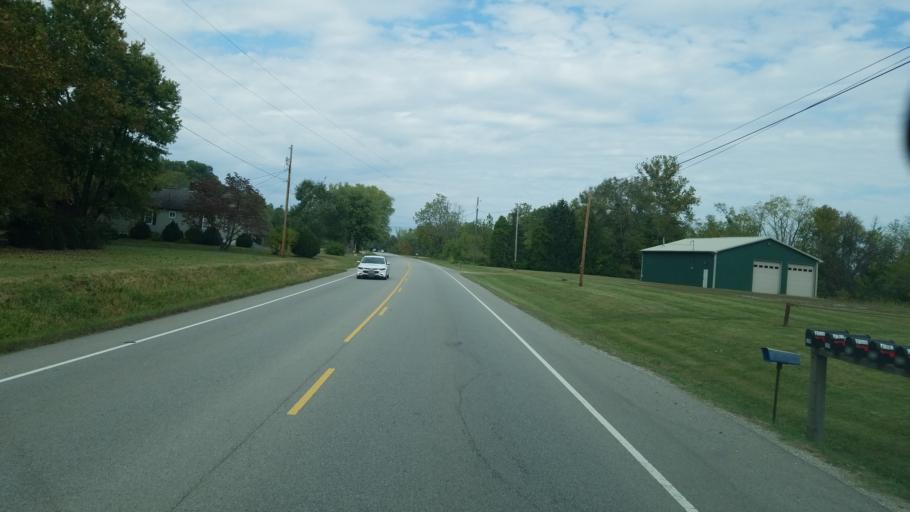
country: US
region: West Virginia
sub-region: Mason County
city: Point Pleasant
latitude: 38.8663
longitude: -82.1426
